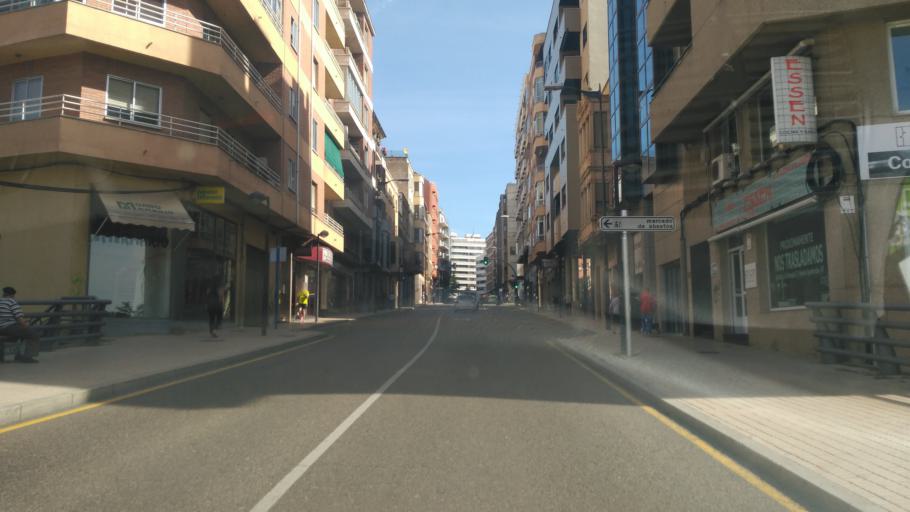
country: ES
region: Castille and Leon
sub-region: Provincia de Zamora
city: Zamora
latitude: 41.5034
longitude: -5.7399
